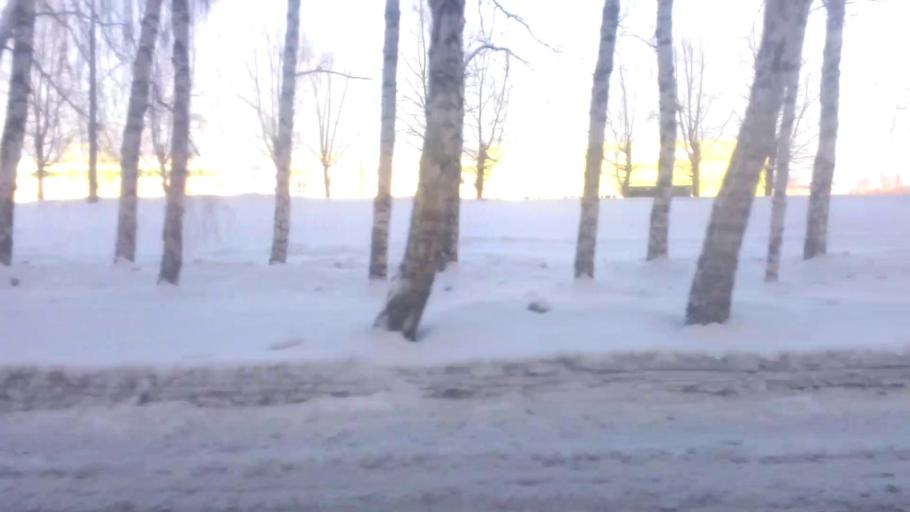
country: RU
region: Altai Krai
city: Novosilikatnyy
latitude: 53.3457
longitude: 83.6547
